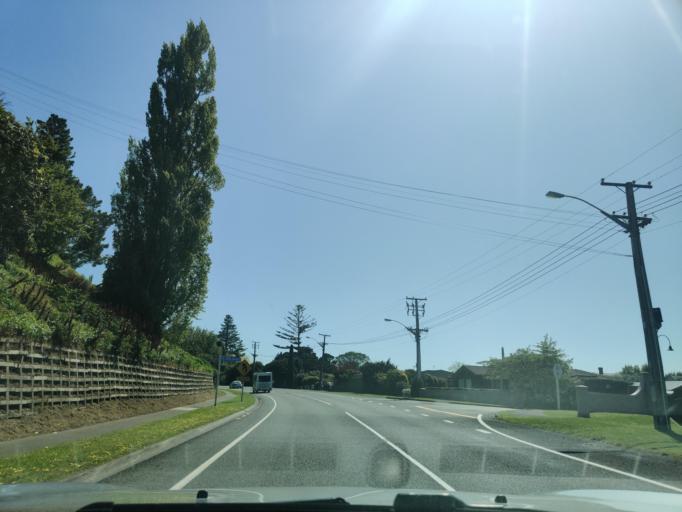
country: NZ
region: Manawatu-Wanganui
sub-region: Wanganui District
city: Wanganui
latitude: -39.9129
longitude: 175.0264
